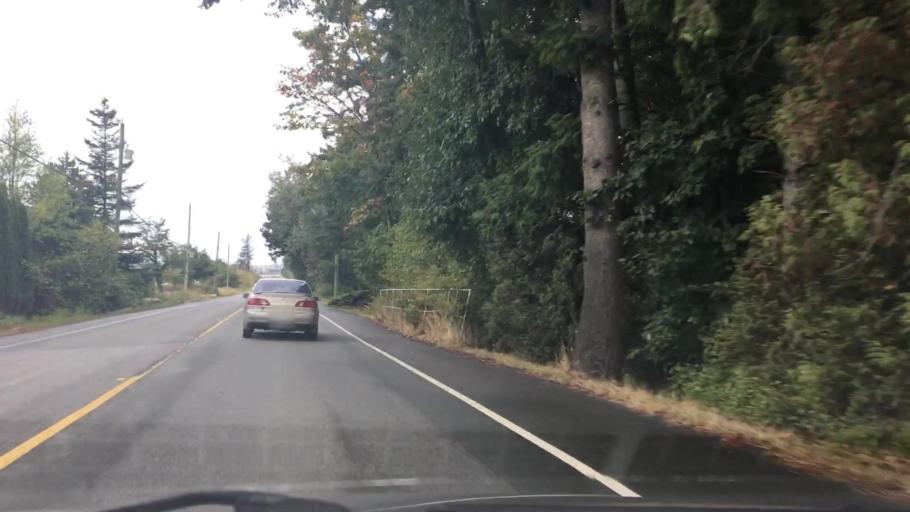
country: CA
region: British Columbia
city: Langley
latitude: 49.1044
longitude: -122.6064
